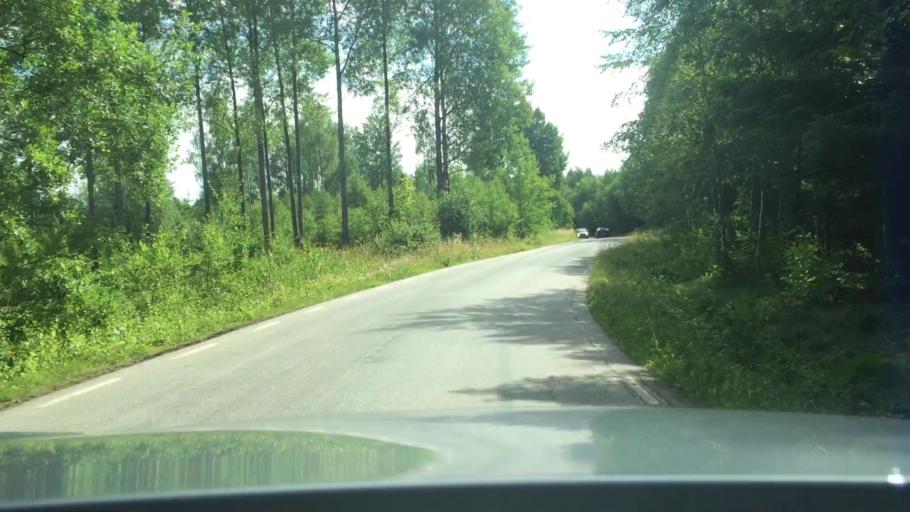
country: SE
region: Vaestra Goetaland
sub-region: Tidaholms Kommun
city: Olofstorp
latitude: 58.3433
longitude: 14.0322
